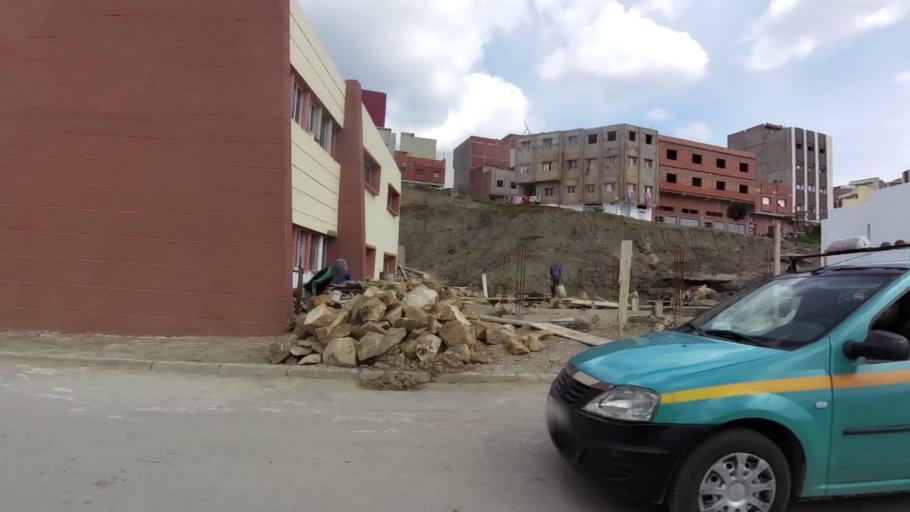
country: MA
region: Tanger-Tetouan
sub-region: Tanger-Assilah
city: Tangier
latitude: 35.7669
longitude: -5.7505
